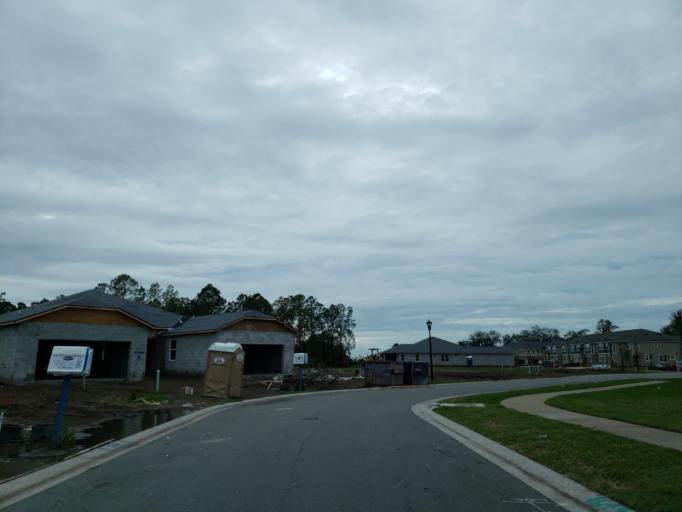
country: US
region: Florida
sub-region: Hillsborough County
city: Riverview
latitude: 27.8511
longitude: -82.3059
